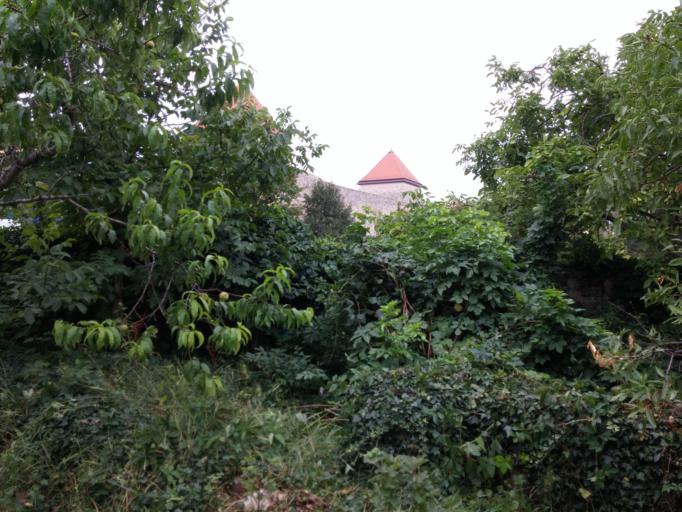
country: HU
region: Veszprem
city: Varpalota
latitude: 47.2021
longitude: 18.1392
